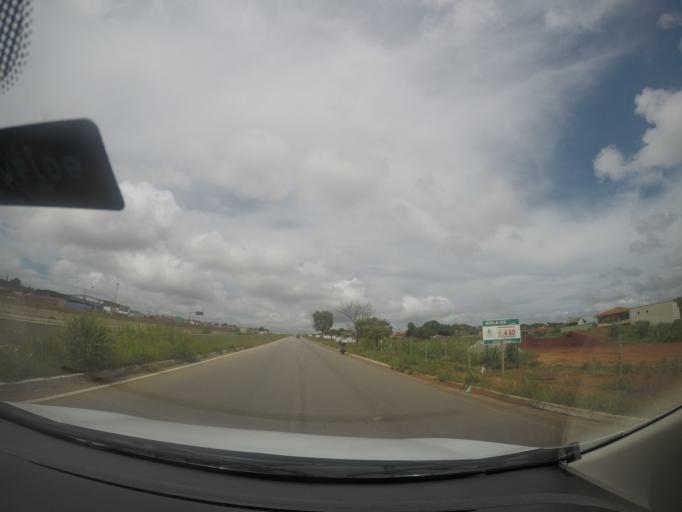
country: BR
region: Goias
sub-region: Goiania
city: Goiania
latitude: -16.7194
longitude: -49.3698
